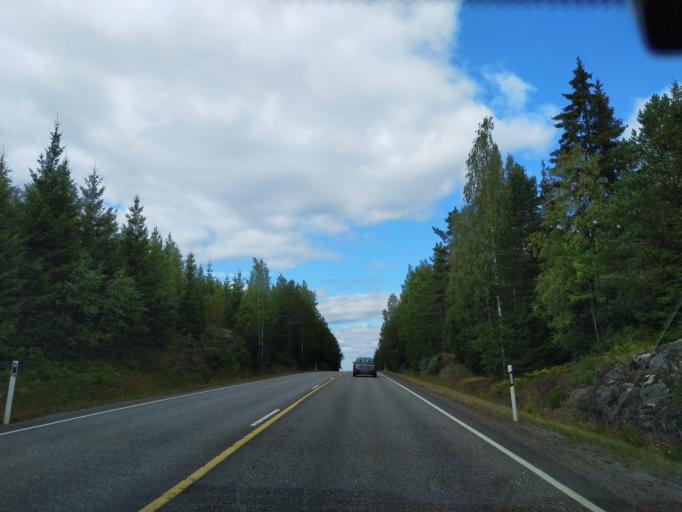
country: FI
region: Haeme
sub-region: Riihimaeki
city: Loppi
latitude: 60.7455
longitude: 24.3460
